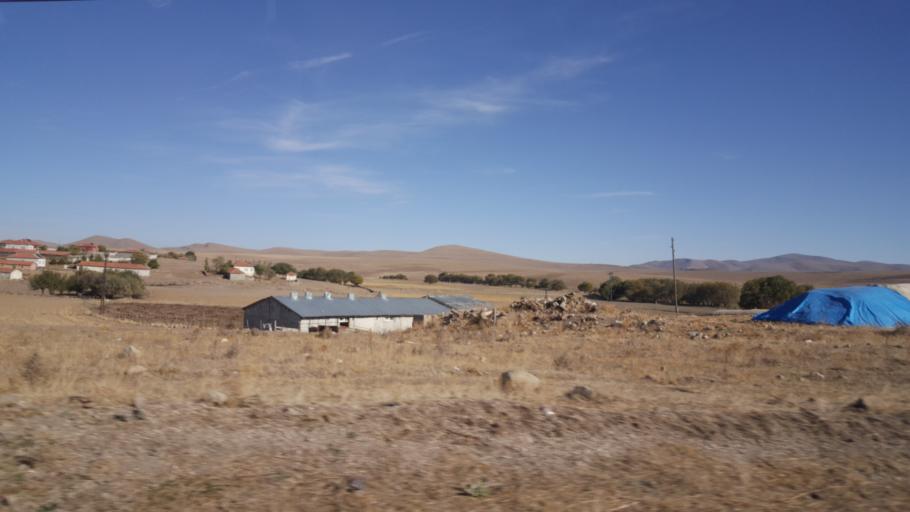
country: TR
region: Ankara
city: Altpinar
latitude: 39.2409
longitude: 32.7433
